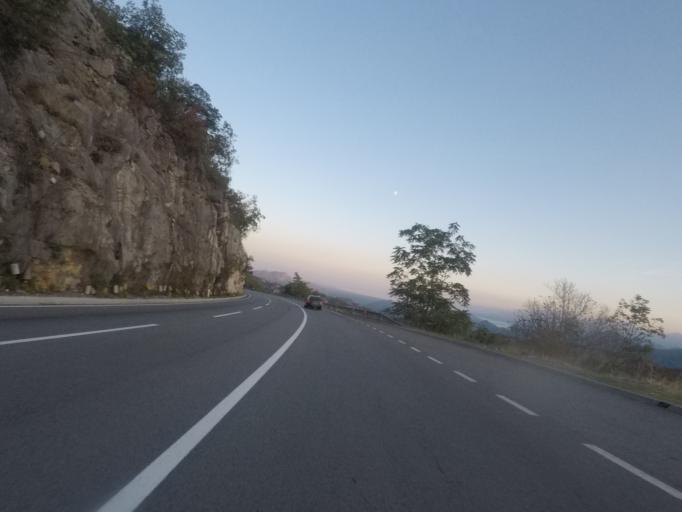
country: ME
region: Cetinje
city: Cetinje
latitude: 42.3756
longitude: 19.0313
